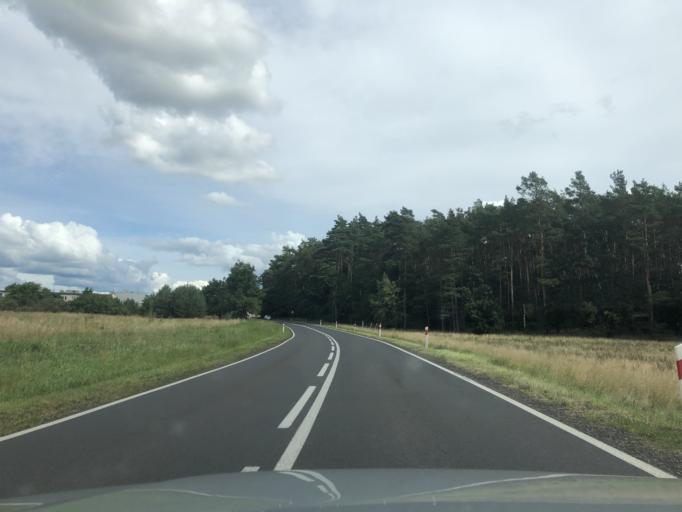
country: PL
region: Greater Poland Voivodeship
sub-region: Powiat pilski
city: Szydlowo
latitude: 53.0760
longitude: 16.5923
